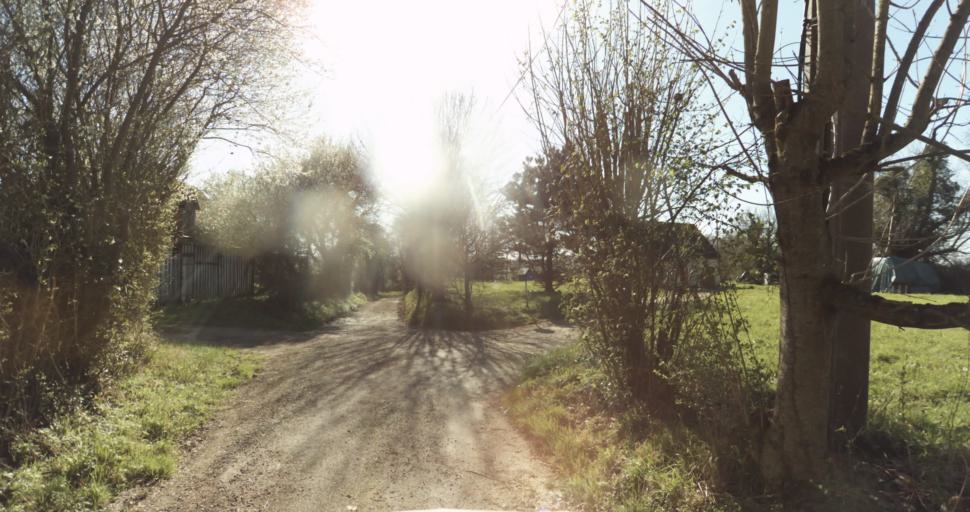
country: FR
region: Lower Normandy
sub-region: Departement du Calvados
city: Saint-Pierre-sur-Dives
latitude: 49.0362
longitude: 0.0451
